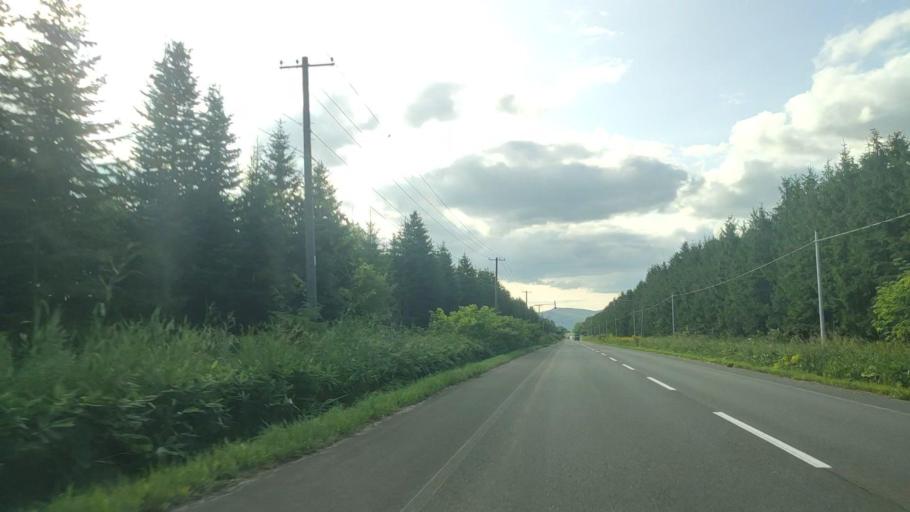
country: JP
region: Hokkaido
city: Makubetsu
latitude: 44.8869
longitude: 142.0081
